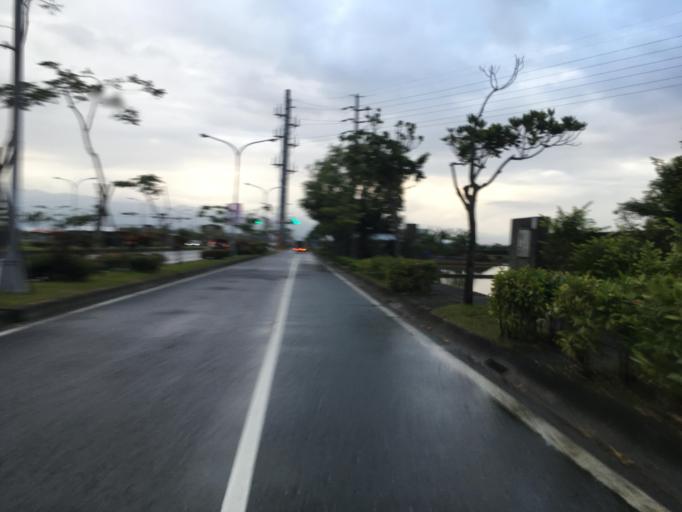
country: TW
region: Taiwan
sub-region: Yilan
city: Yilan
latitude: 24.7296
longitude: 121.7721
